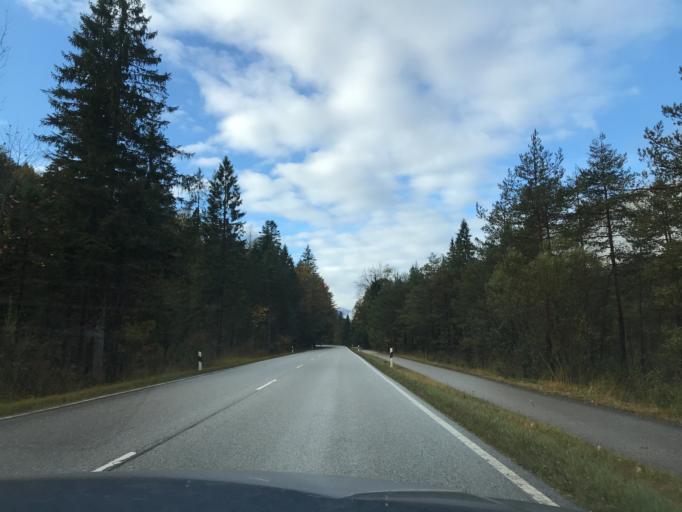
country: DE
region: Bavaria
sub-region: Upper Bavaria
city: Lenggries
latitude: 47.6182
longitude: 11.5913
